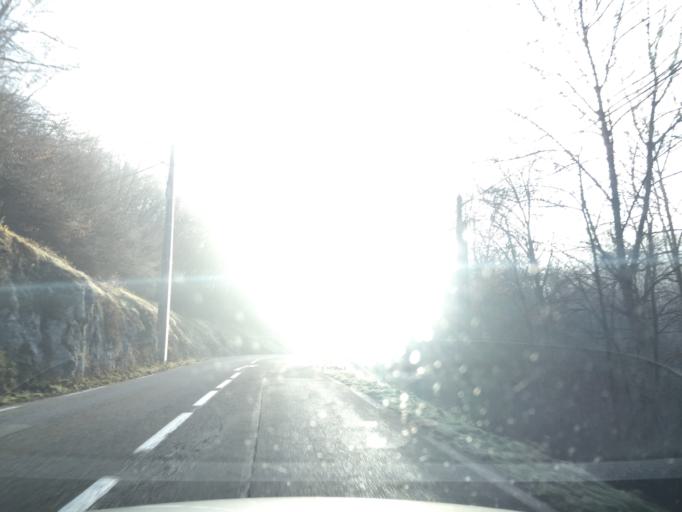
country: FR
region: Rhone-Alpes
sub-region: Departement de la Haute-Savoie
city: Gruffy
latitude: 45.7231
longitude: 6.0979
